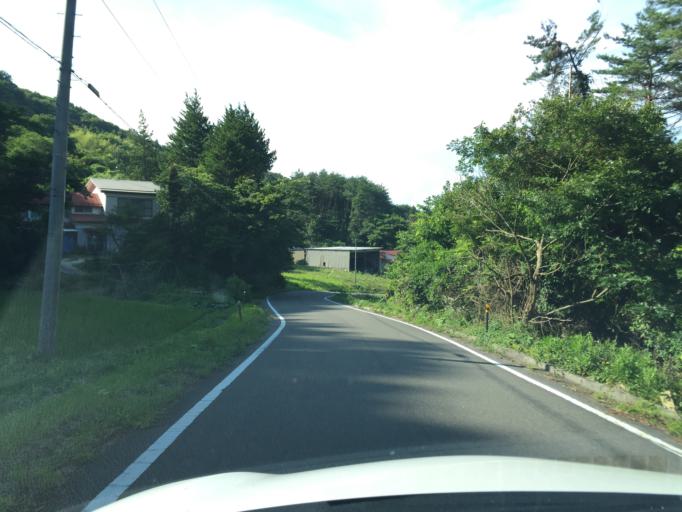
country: JP
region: Fukushima
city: Sukagawa
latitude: 37.2628
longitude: 140.4999
